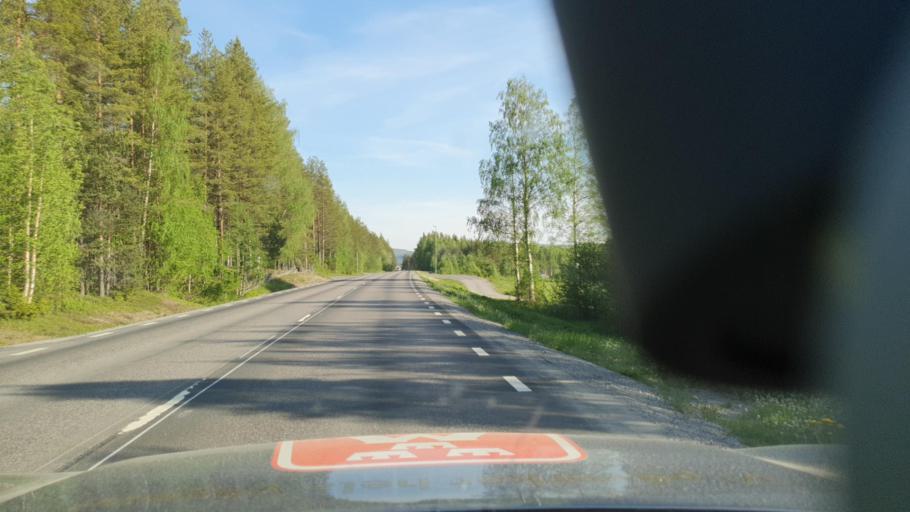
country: SE
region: Norrbotten
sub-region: Bodens Kommun
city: Boden
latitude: 65.8747
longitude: 21.4101
